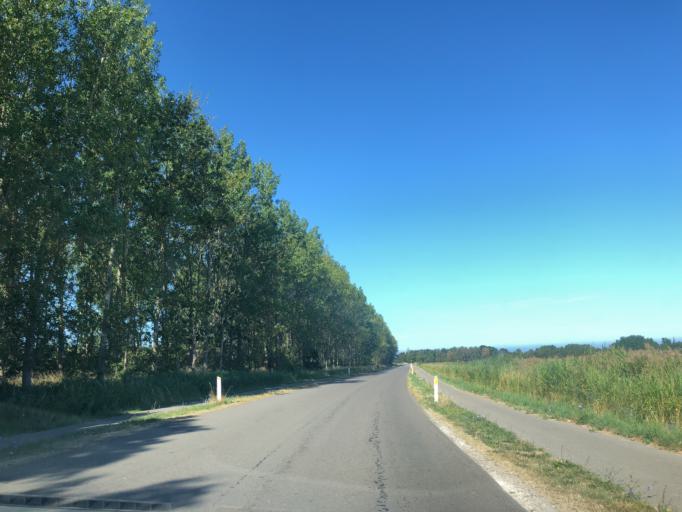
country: DK
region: Zealand
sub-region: Slagelse Kommune
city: Forlev
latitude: 55.3745
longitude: 11.2376
